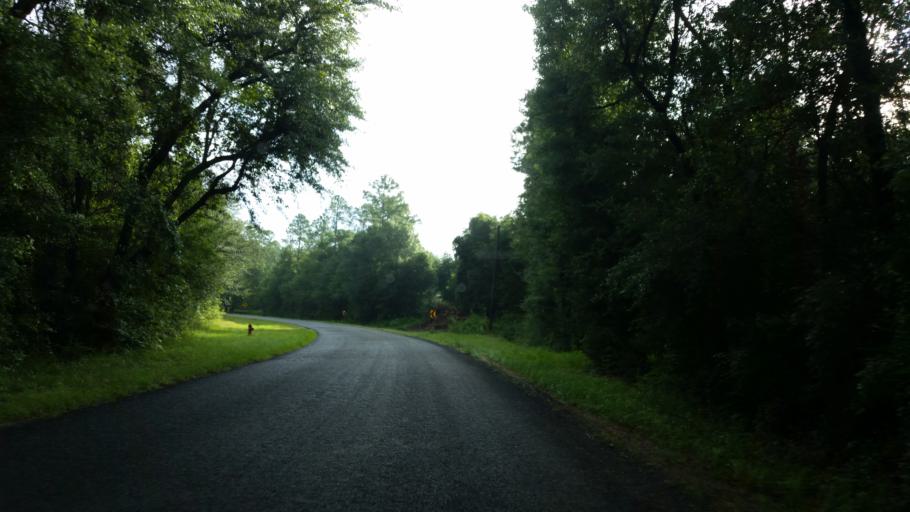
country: US
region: Florida
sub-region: Okaloosa County
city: Crestview
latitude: 30.6758
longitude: -86.7504
